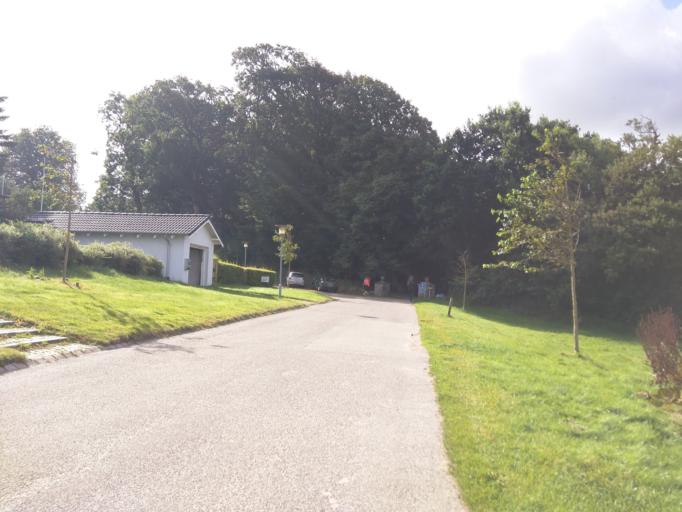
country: DK
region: Central Jutland
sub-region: Viborg Kommune
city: Viborg
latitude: 56.4481
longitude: 9.4237
